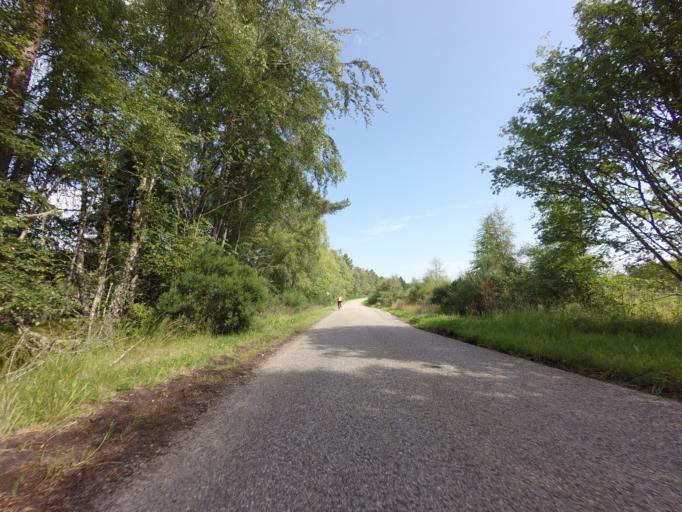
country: GB
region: Scotland
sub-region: Highland
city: Invergordon
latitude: 57.7335
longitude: -4.1911
